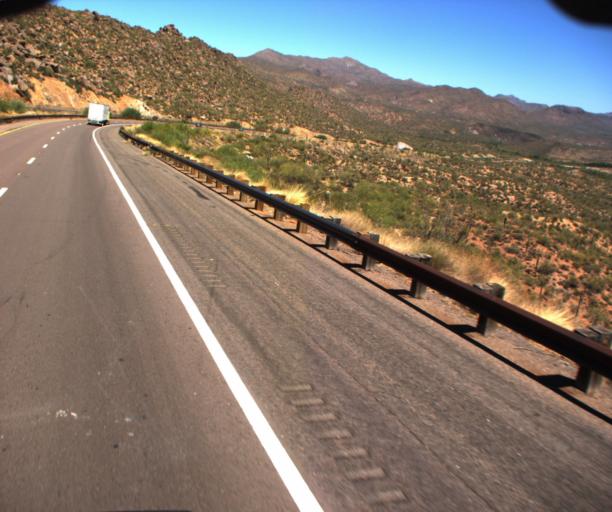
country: US
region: Arizona
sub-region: Maricopa County
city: Rio Verde
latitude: 33.7107
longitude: -111.5077
